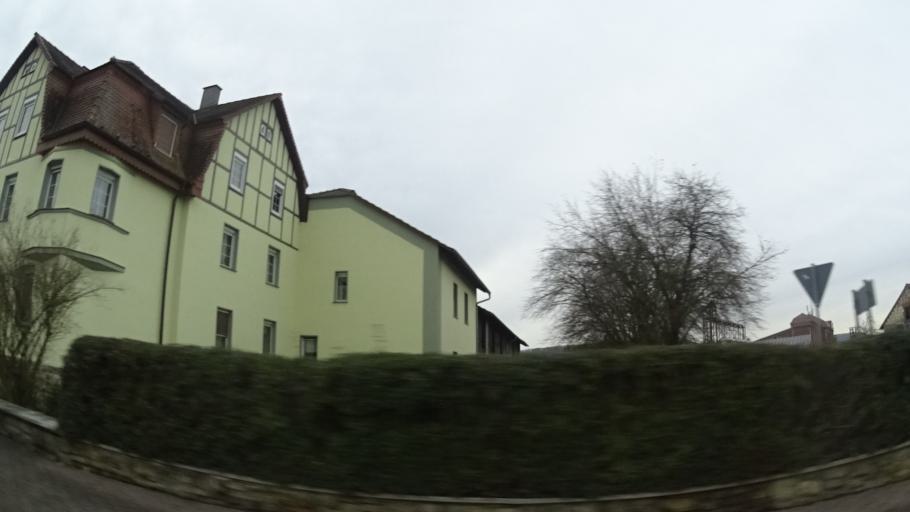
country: DE
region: Thuringia
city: Buttlar
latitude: 50.7585
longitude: 9.9540
